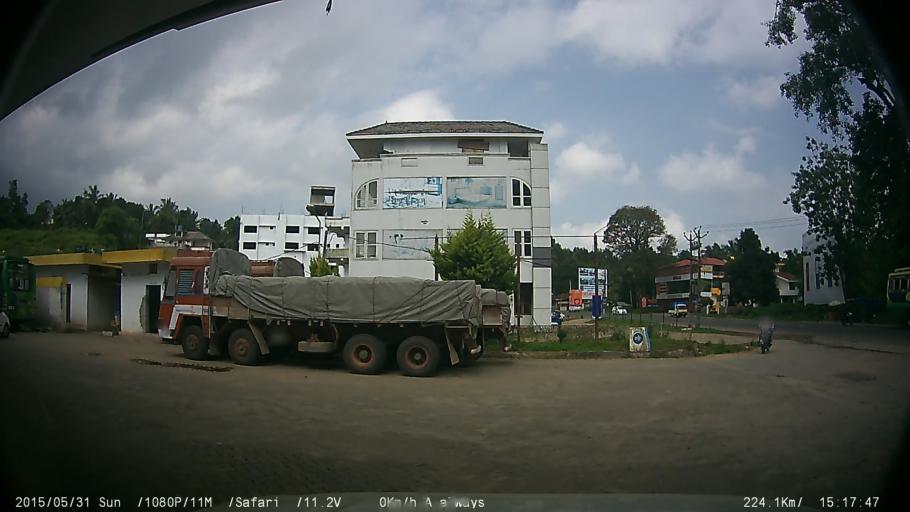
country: IN
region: Kerala
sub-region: Wayanad
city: Panamaram
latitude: 11.6589
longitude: 76.2459
